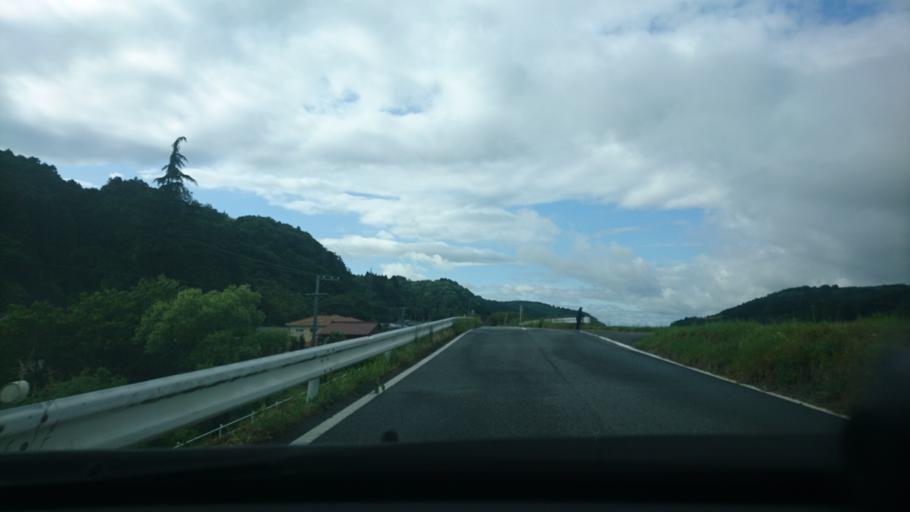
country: JP
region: Miyagi
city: Wakuya
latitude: 38.6596
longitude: 141.2858
